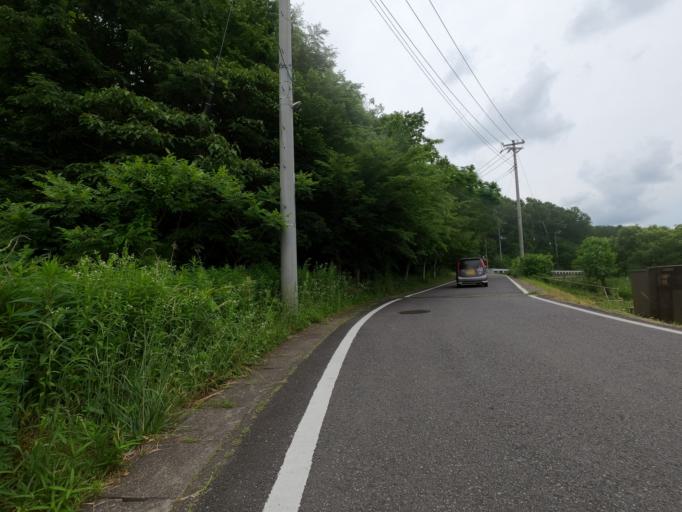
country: JP
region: Ibaraki
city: Moriya
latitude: 35.9566
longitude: 139.9663
